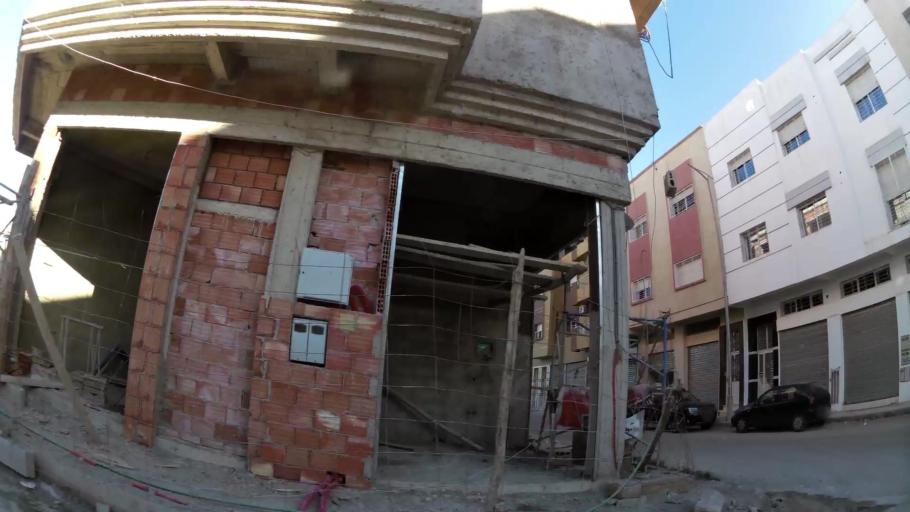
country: MA
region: Fes-Boulemane
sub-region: Fes
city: Fes
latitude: 34.0077
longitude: -5.0106
